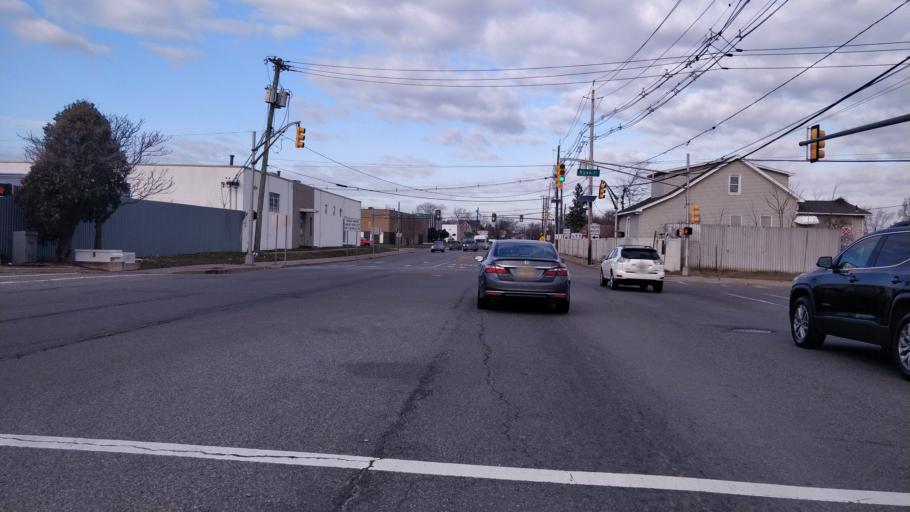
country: US
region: New Jersey
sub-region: Middlesex County
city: South Plainfield
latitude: 40.5616
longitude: -74.4179
